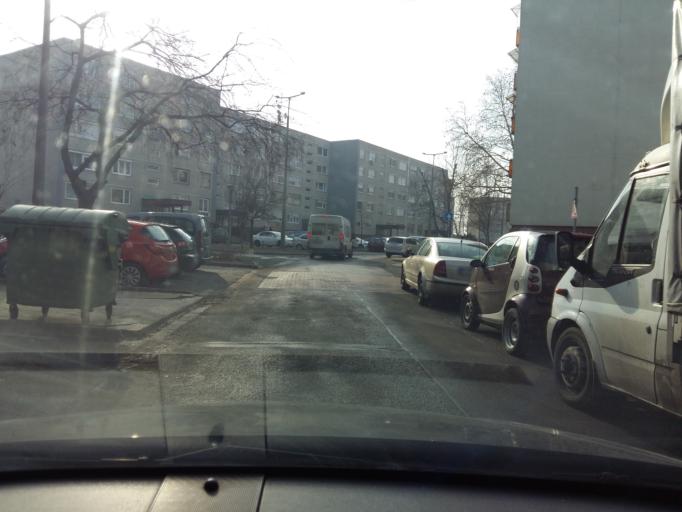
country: HU
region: Pest
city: Szigetszentmiklos
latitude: 47.3415
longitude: 19.0341
